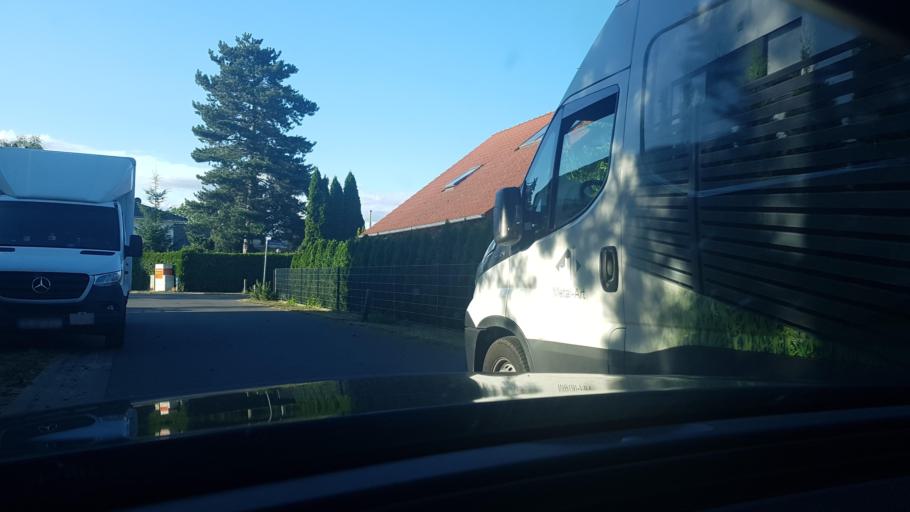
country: DE
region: Brandenburg
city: Neuenhagen
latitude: 52.5164
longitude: 13.7202
